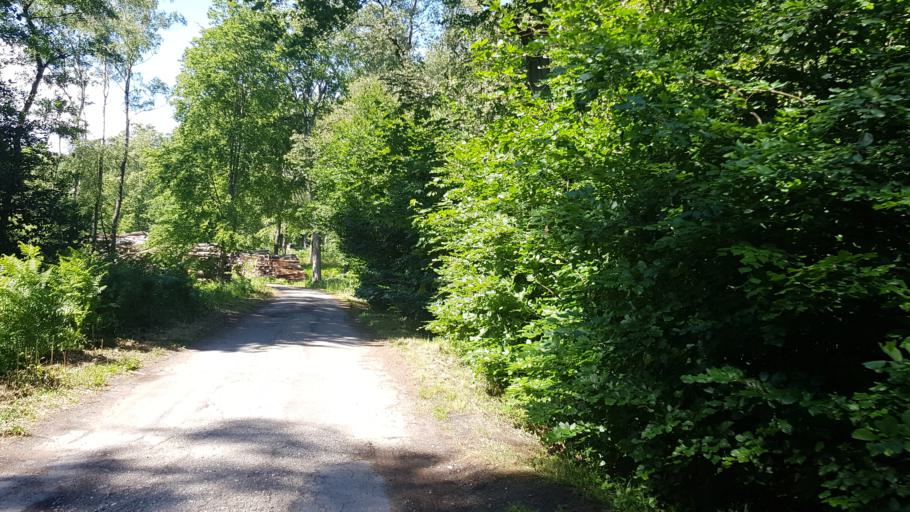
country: DE
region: North Rhine-Westphalia
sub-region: Regierungsbezirk Dusseldorf
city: Duisburg
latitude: 51.3961
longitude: 6.8244
